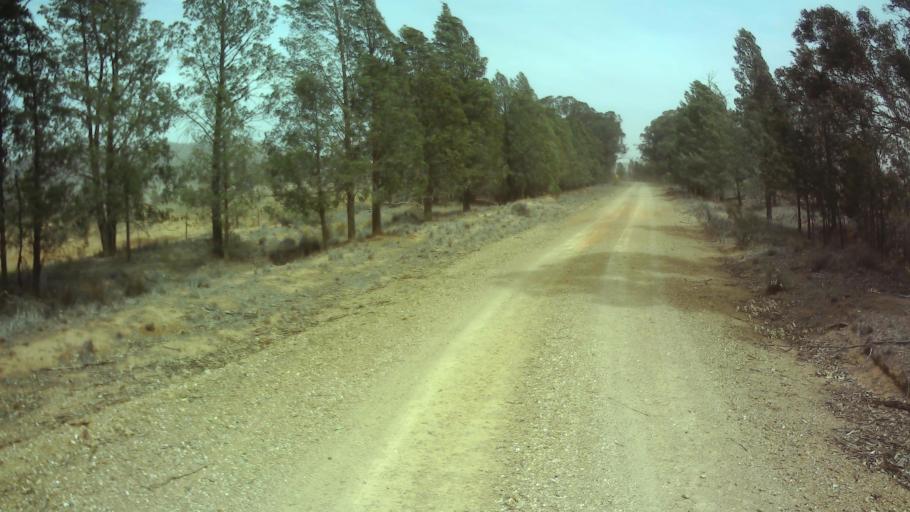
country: AU
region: New South Wales
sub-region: Weddin
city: Grenfell
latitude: -33.7181
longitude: 147.9687
